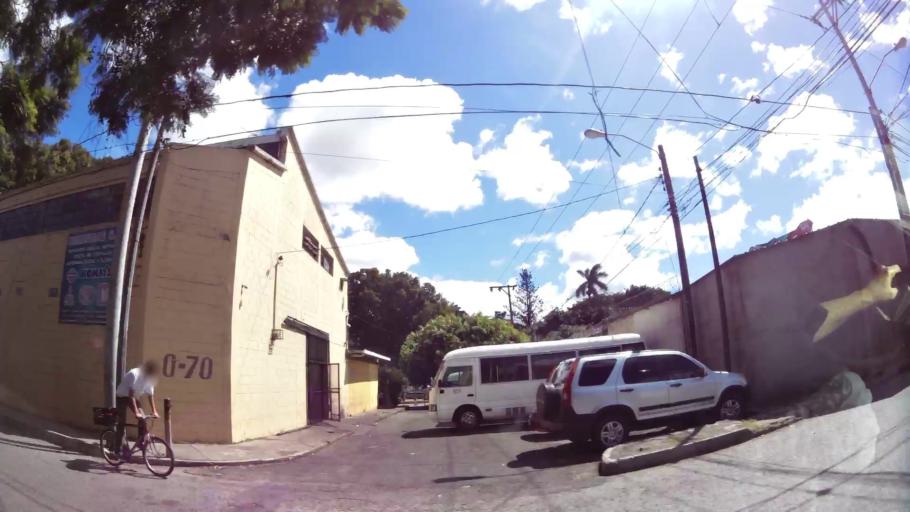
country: GT
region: Guatemala
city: Guatemala City
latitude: 14.6025
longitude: -90.5289
